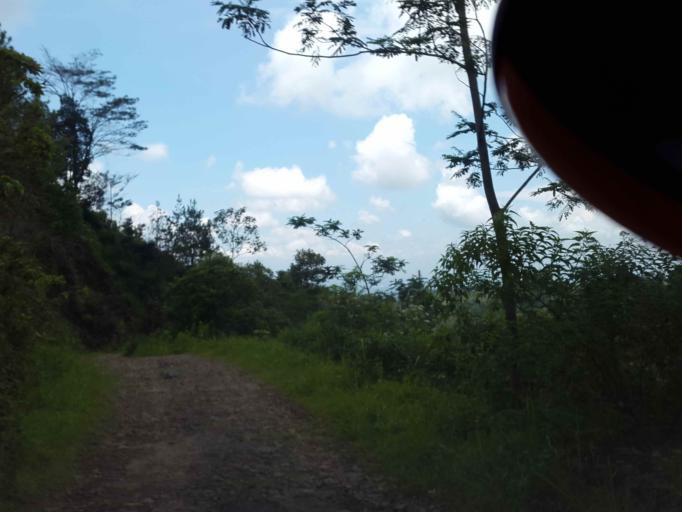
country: ID
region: Central Java
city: Jatiroto
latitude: -7.7143
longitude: 111.1195
